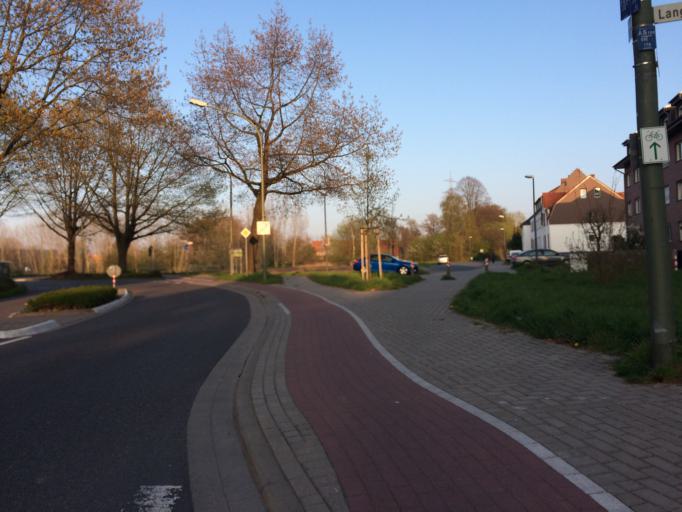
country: DE
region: Lower Saxony
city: Osnabrueck
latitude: 52.2565
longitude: 8.0838
